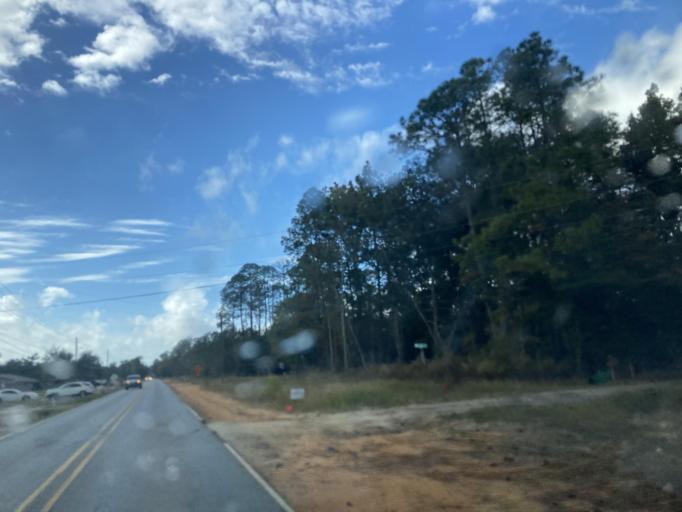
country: US
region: Mississippi
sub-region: Jackson County
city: Gulf Hills
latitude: 30.4390
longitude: -88.8259
